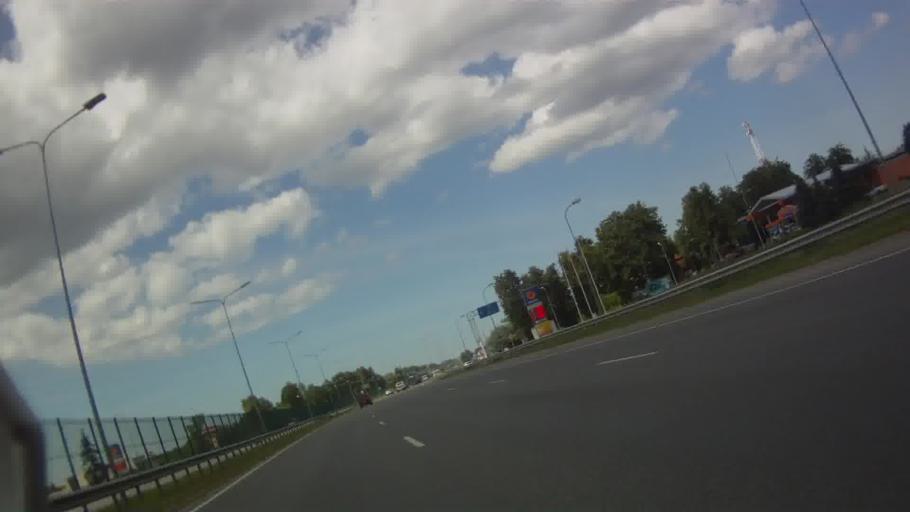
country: LV
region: Marupe
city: Marupe
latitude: 56.9333
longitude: 24.0063
